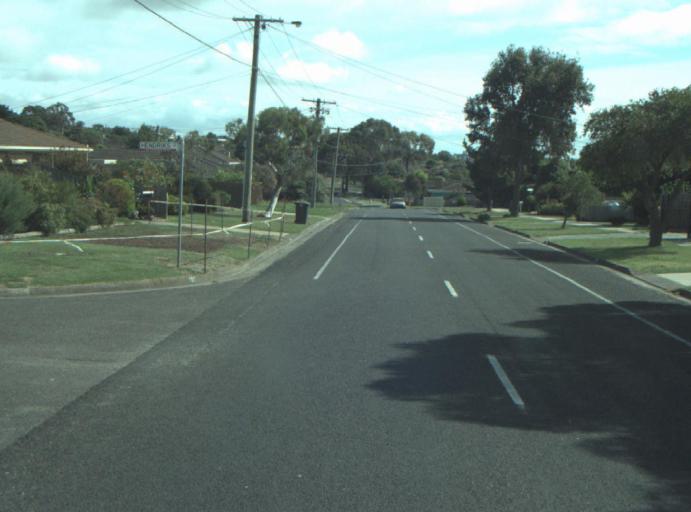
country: AU
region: Victoria
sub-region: Greater Geelong
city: Wandana Heights
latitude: -38.1850
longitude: 144.3207
